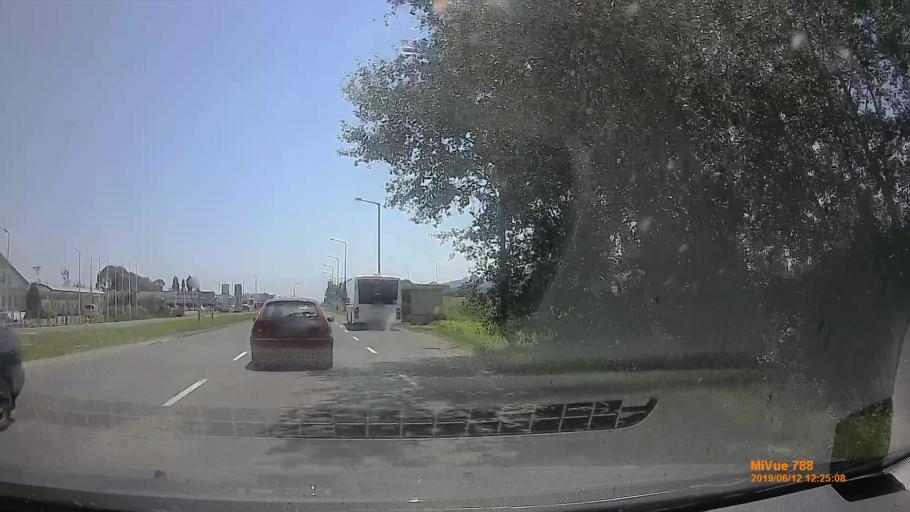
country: HU
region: Bacs-Kiskun
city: Kecskemet
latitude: 46.8842
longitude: 19.7053
